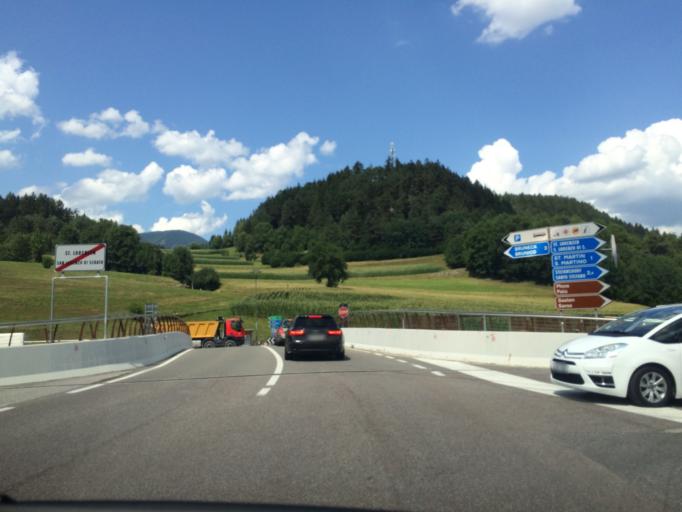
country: IT
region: Trentino-Alto Adige
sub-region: Bolzano
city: San Lorenzo di Sebato
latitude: 46.7838
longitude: 11.8960
